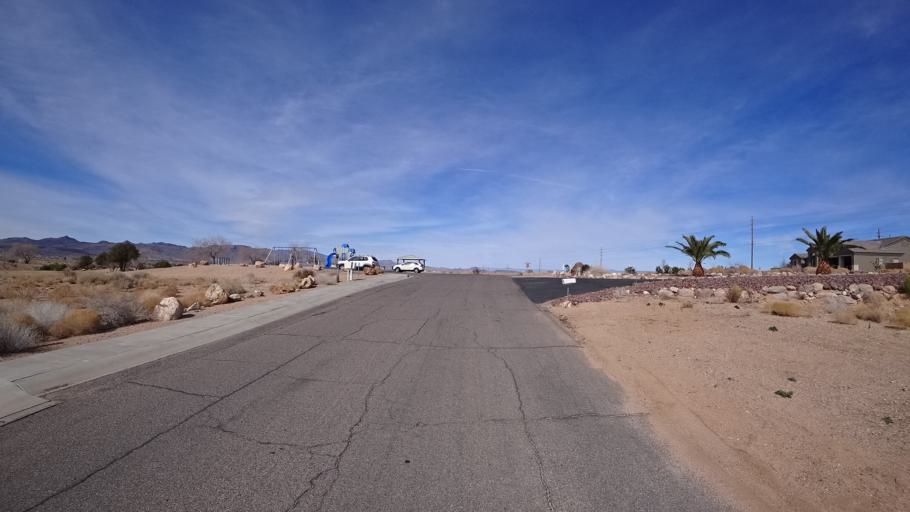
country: US
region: Arizona
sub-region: Mohave County
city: Kingman
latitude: 35.1949
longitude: -113.9883
